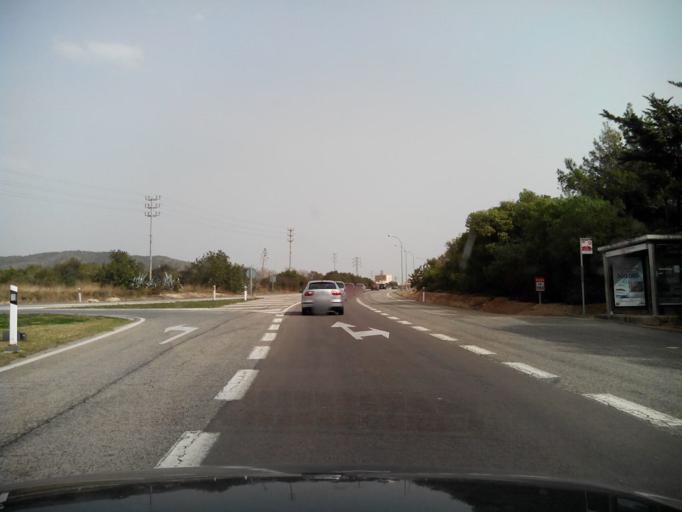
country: ES
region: Catalonia
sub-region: Provincia de Tarragona
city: Roda de Bara
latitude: 41.1733
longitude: 1.4694
